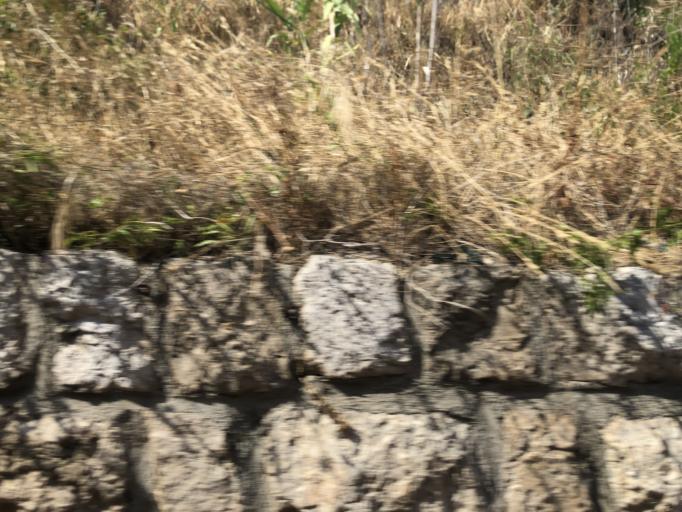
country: FR
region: Provence-Alpes-Cote d'Azur
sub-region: Departement des Alpes-Maritimes
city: Beaulieu-sur-Mer
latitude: 43.7104
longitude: 7.3266
